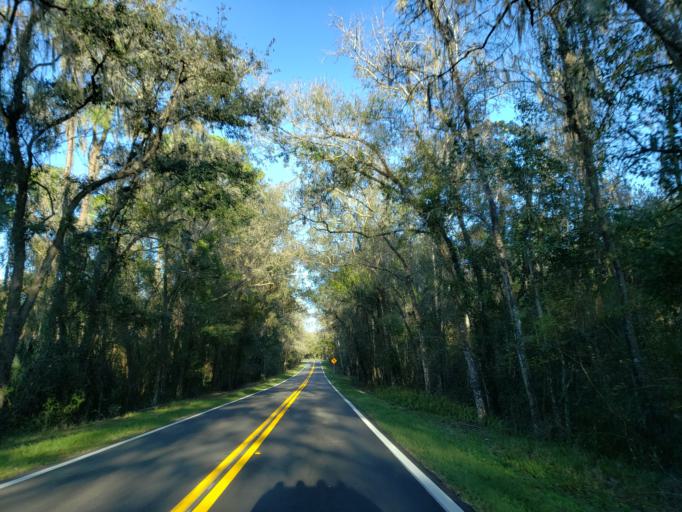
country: US
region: Florida
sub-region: Hillsborough County
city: Boyette
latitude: 27.8234
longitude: -82.2025
